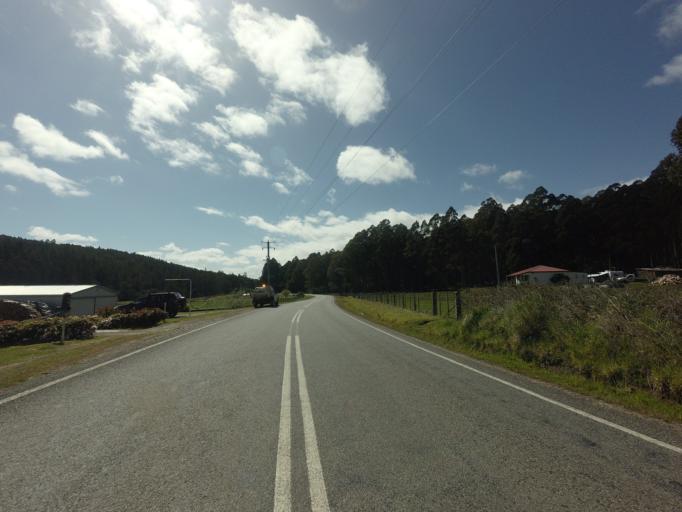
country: AU
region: Tasmania
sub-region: Derwent Valley
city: New Norfolk
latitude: -42.7238
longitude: 146.6771
